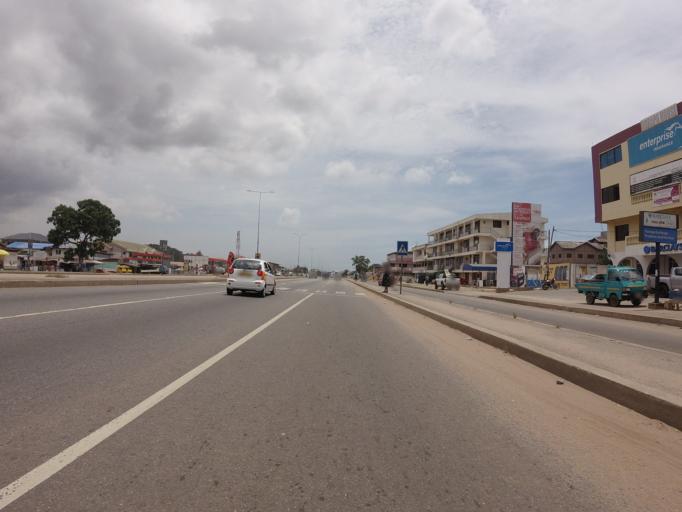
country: GH
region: Greater Accra
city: Accra
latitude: 5.5737
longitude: -0.2502
